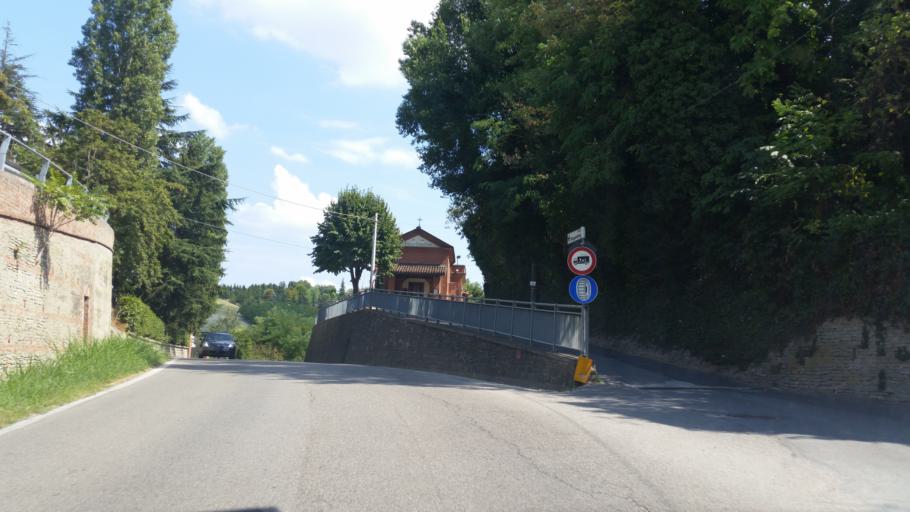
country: IT
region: Piedmont
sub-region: Provincia di Cuneo
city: Alba
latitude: 44.6944
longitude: 8.0491
